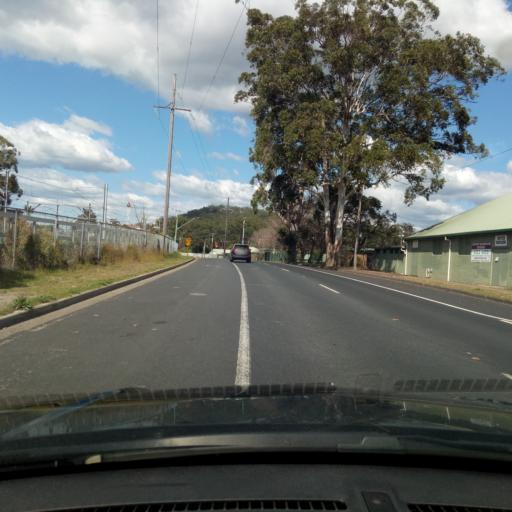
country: AU
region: New South Wales
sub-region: Gosford Shire
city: Gosford
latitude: -33.4135
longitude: 151.3430
